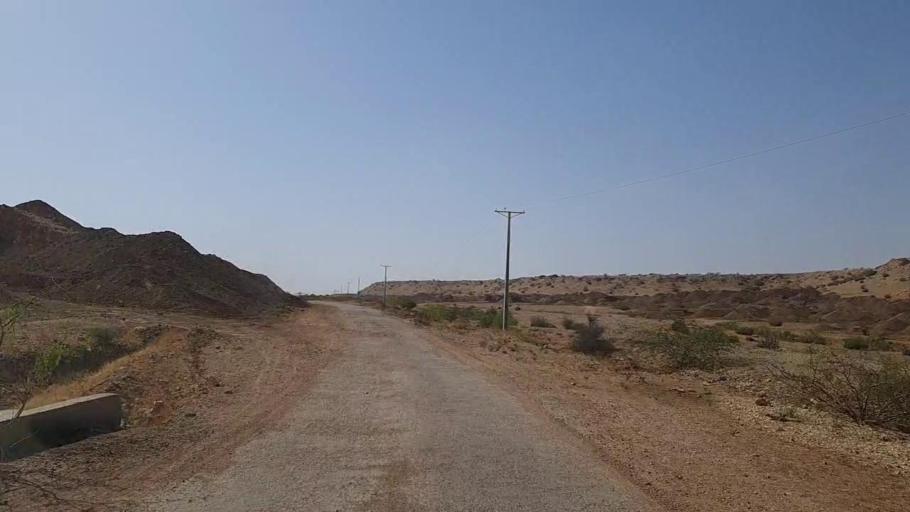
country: PK
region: Sindh
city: Kotri
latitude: 25.1622
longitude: 68.2127
